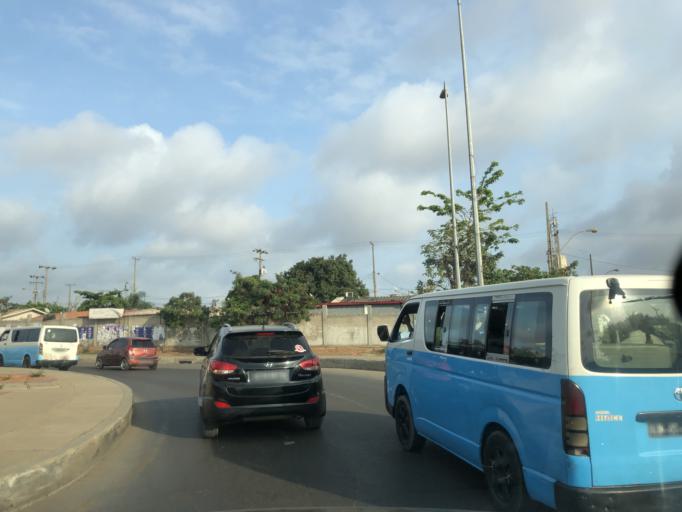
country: AO
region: Luanda
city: Luanda
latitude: -8.8956
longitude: 13.2146
